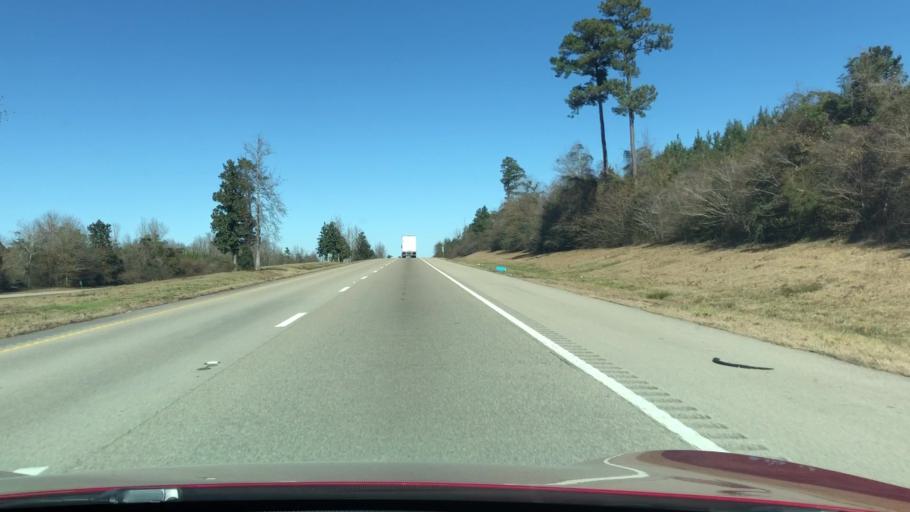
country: US
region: Mississippi
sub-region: Pearl River County
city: Poplarville
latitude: 30.7681
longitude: -89.5211
